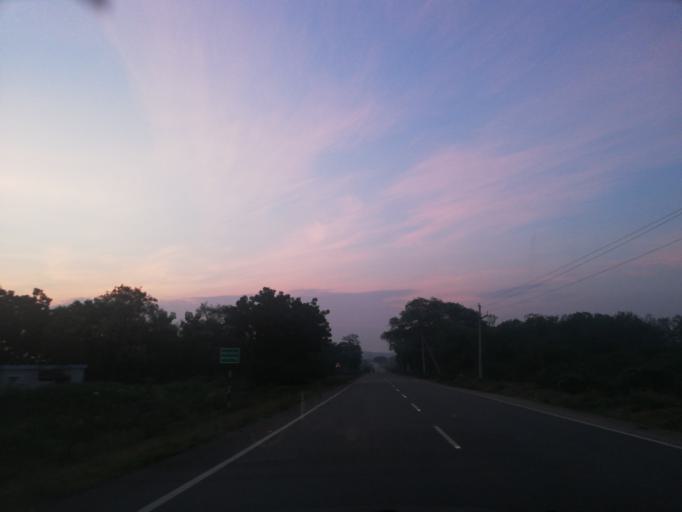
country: IN
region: Andhra Pradesh
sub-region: Guntur
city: Macherla
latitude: 16.6838
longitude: 79.2569
